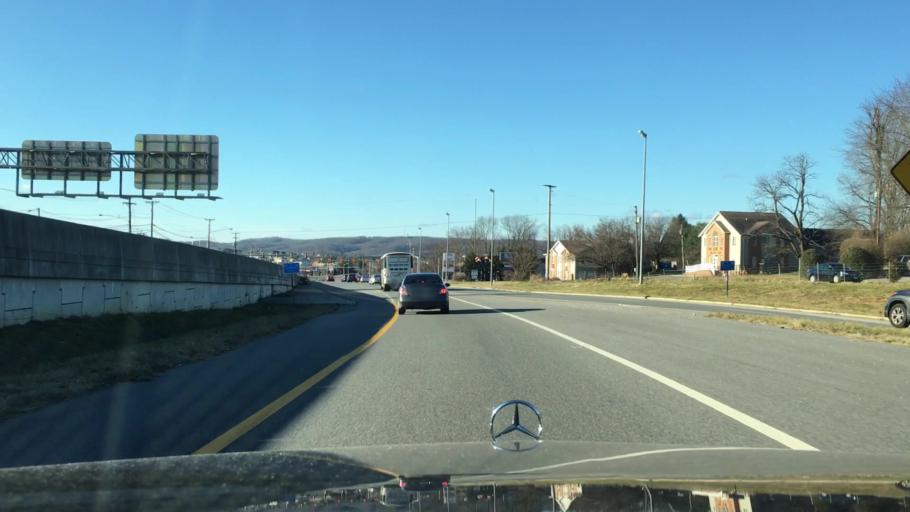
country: US
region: Virginia
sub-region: Montgomery County
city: Christiansburg
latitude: 37.1565
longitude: -80.4165
